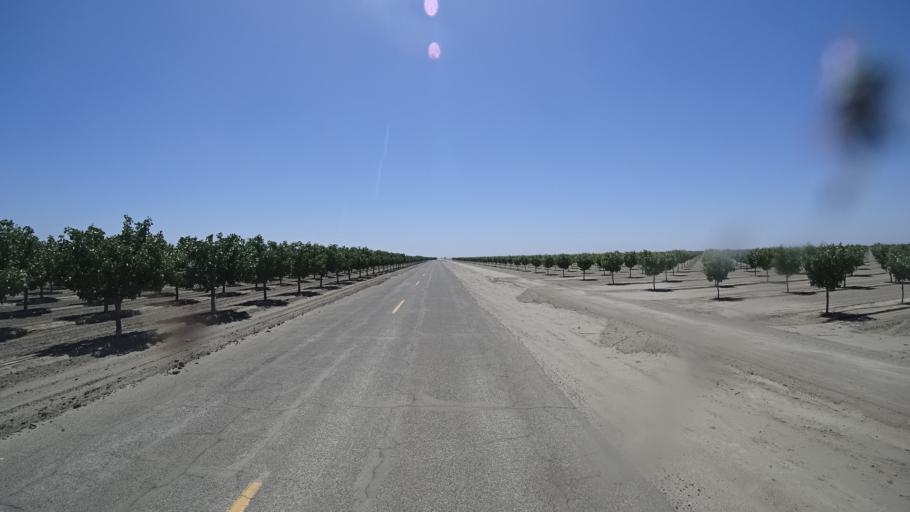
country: US
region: California
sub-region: Kings County
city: Corcoran
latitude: 36.1014
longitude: -119.5989
